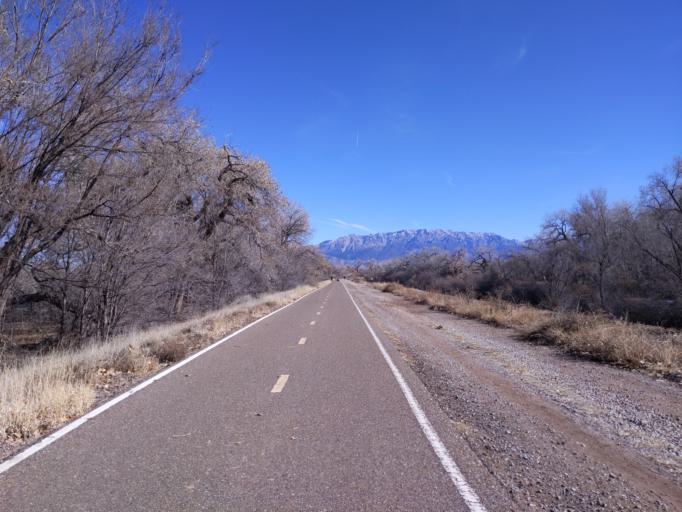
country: US
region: New Mexico
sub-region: Bernalillo County
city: Los Ranchos de Albuquerque
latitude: 35.1616
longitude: -106.6643
